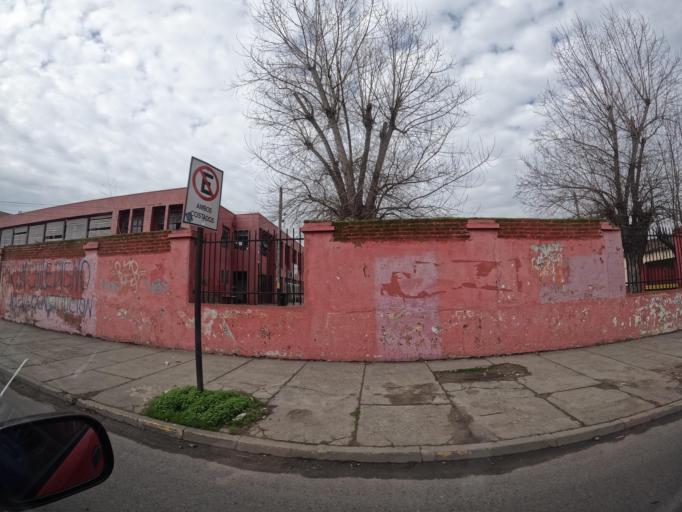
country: CL
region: Maule
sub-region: Provincia de Linares
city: Linares
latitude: -35.8503
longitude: -71.5893
